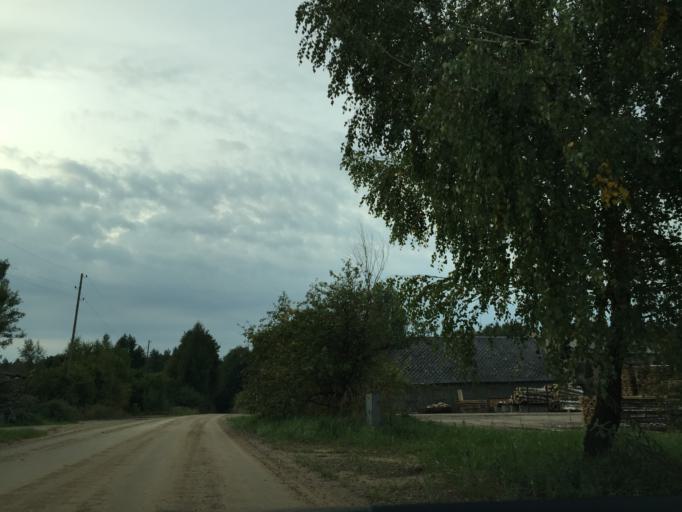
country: LV
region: Ogre
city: Ogre
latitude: 56.8245
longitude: 24.6561
